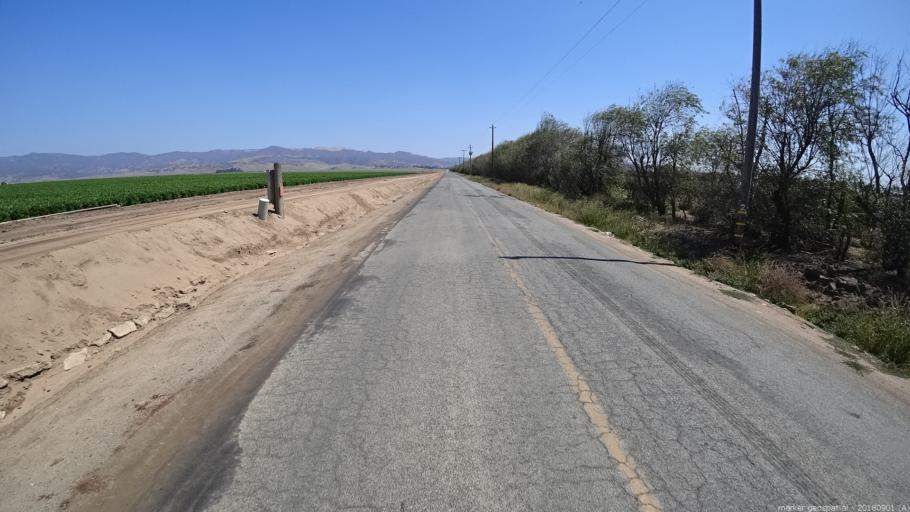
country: US
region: California
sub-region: Monterey County
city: Chualar
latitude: 36.5769
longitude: -121.4930
